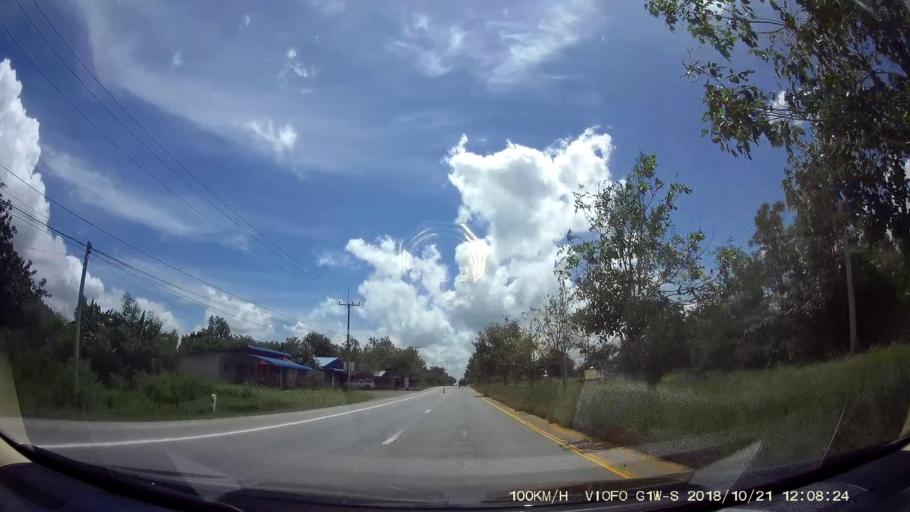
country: TH
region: Chaiyaphum
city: Chatturat
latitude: 15.4340
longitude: 101.8305
